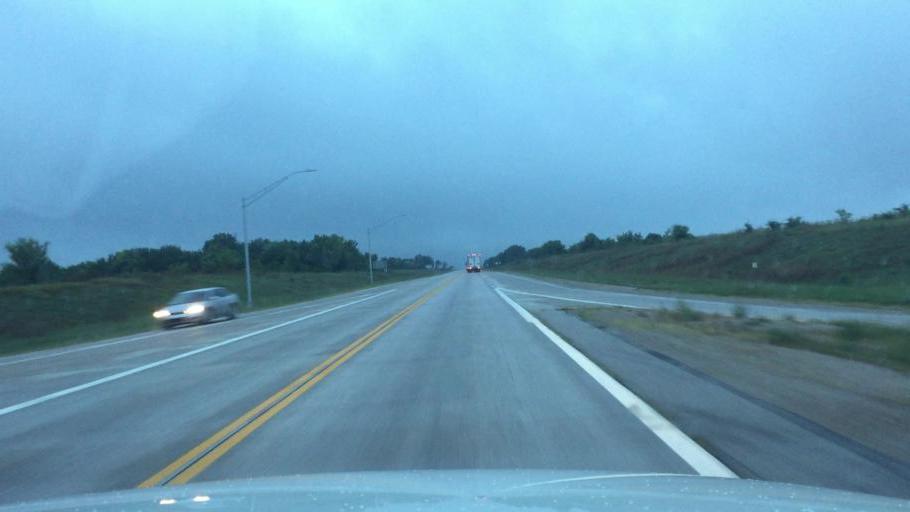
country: US
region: Kansas
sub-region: Neosho County
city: Chanute
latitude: 37.6436
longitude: -95.4797
